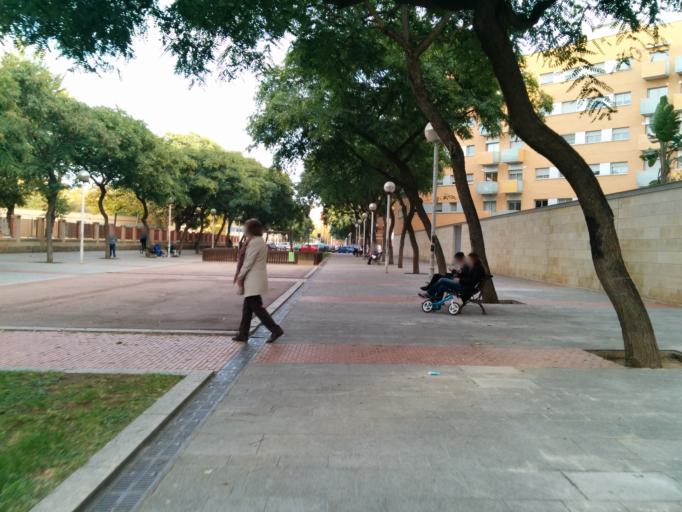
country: ES
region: Catalonia
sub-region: Provincia de Barcelona
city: Ciutat Vella
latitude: 41.3928
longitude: 2.1943
